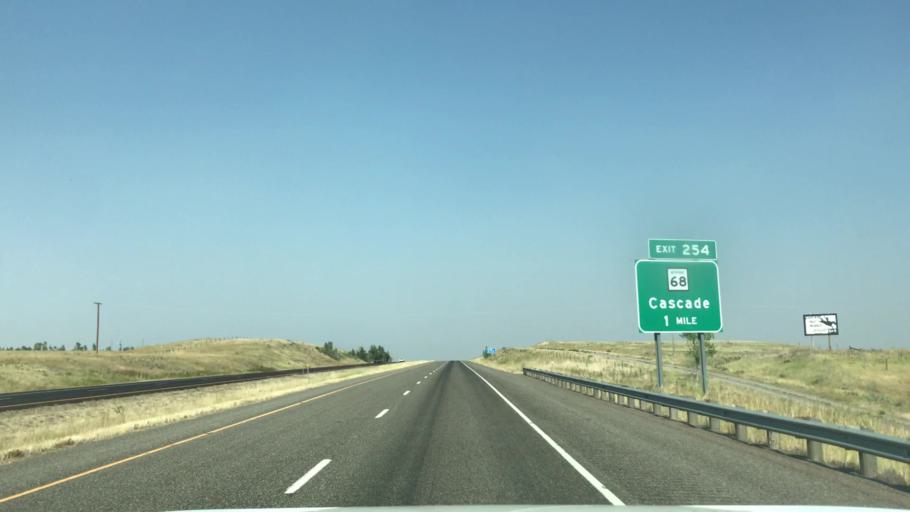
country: US
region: Montana
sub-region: Cascade County
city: Sun Prairie
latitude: 47.2451
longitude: -111.7202
